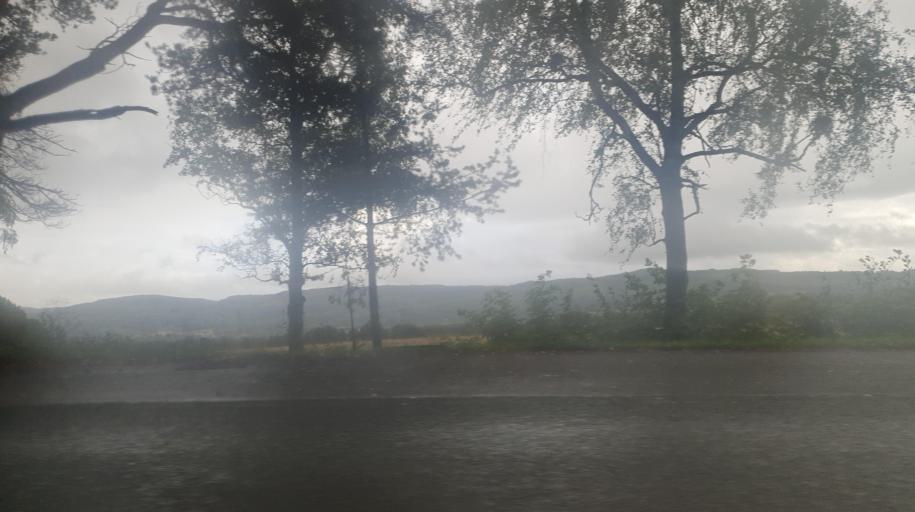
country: NO
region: Nord-Trondelag
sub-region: Verdal
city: Verdal
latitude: 63.7942
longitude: 11.5493
